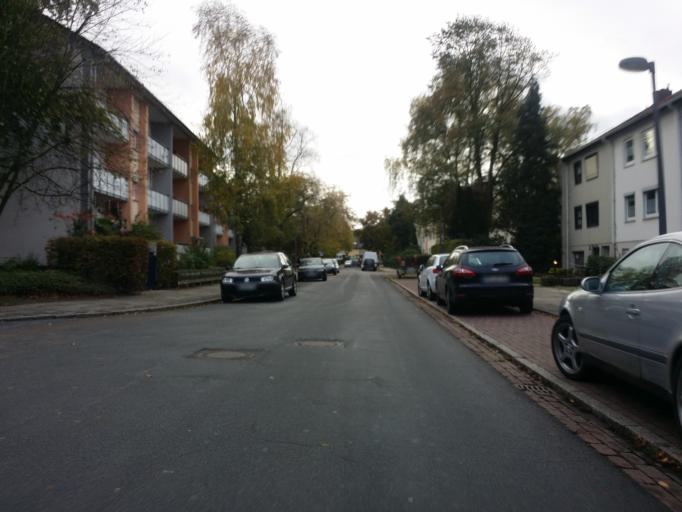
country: DE
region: Lower Saxony
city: Stuhr
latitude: 53.0400
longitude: 8.7318
